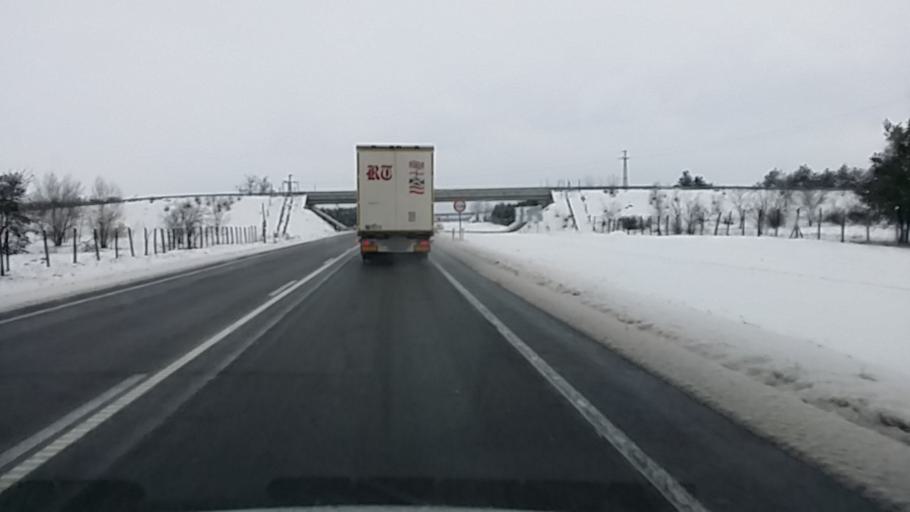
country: HU
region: Gyor-Moson-Sopron
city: Rajka
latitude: 47.9559
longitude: 17.1680
